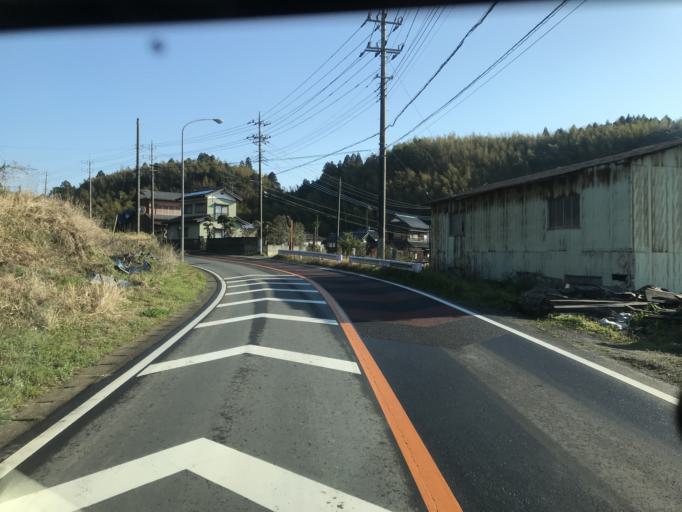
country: JP
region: Chiba
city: Sawara
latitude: 35.8770
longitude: 140.4957
